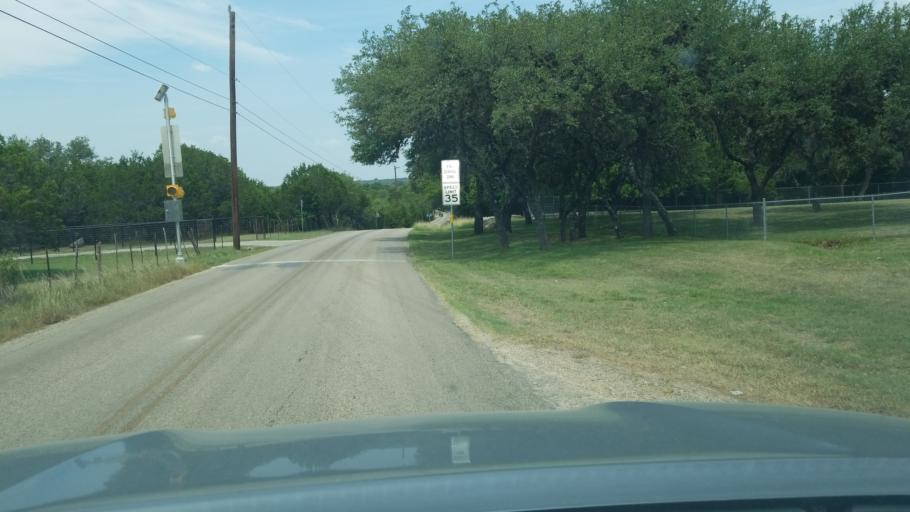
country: US
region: Texas
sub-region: Comal County
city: Bulverde
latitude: 29.7598
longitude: -98.4627
